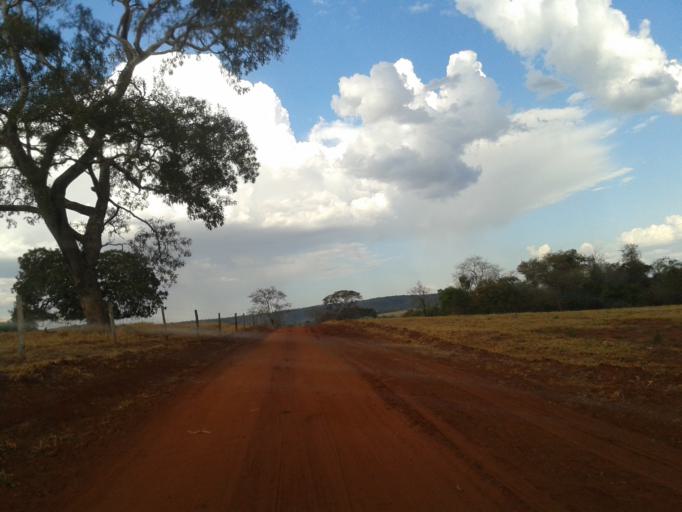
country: BR
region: Minas Gerais
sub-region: Santa Vitoria
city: Santa Vitoria
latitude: -19.1703
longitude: -49.9512
